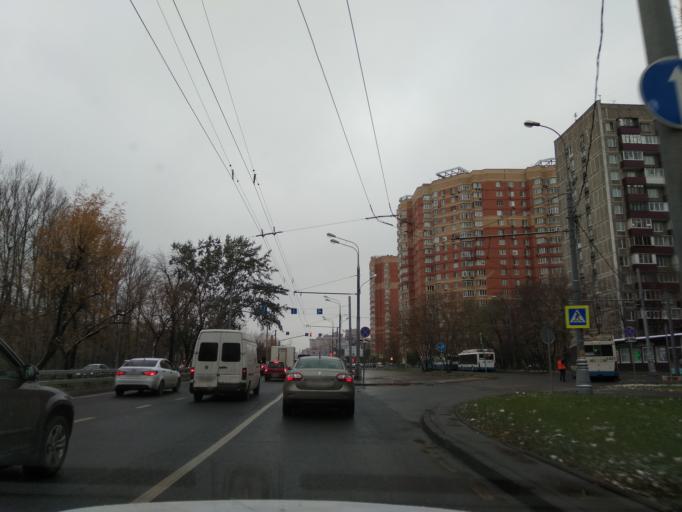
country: RU
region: Moscow
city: Likhobory
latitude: 55.8413
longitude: 37.5512
